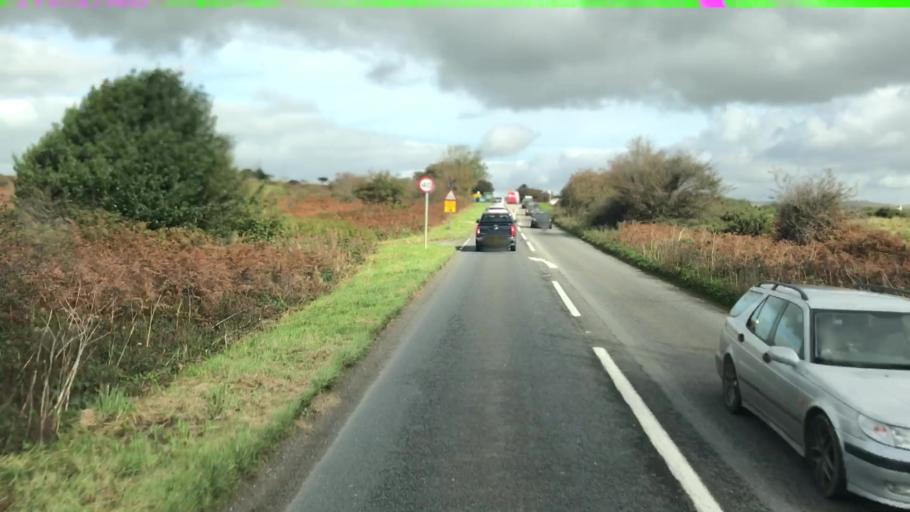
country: GB
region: England
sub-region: Devon
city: Yelverton
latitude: 50.4540
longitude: -4.1062
